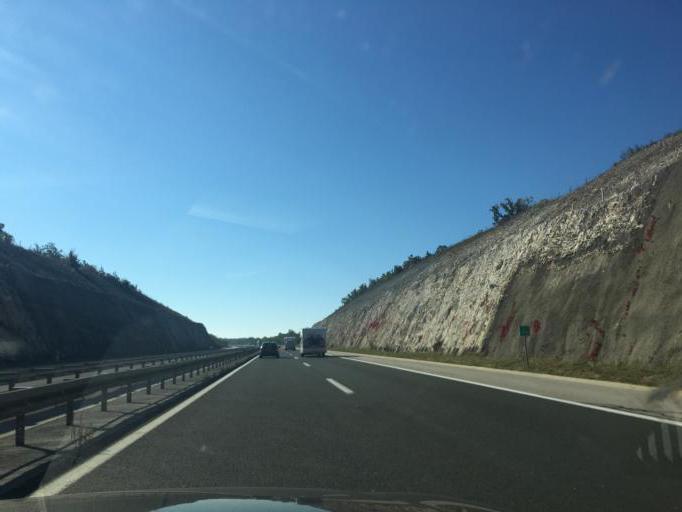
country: HR
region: Licko-Senjska
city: Gospic
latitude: 44.7196
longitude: 15.3862
